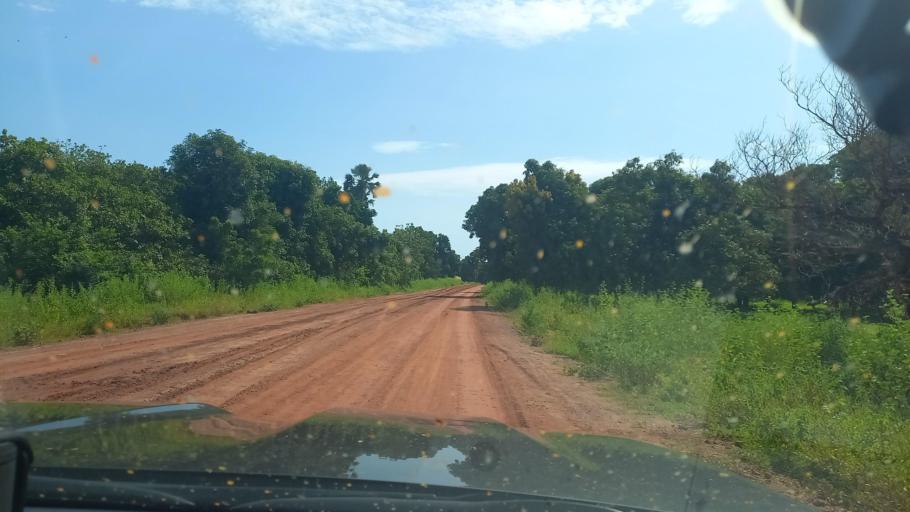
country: SN
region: Ziguinchor
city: Adeane
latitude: 12.6677
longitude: -16.0994
